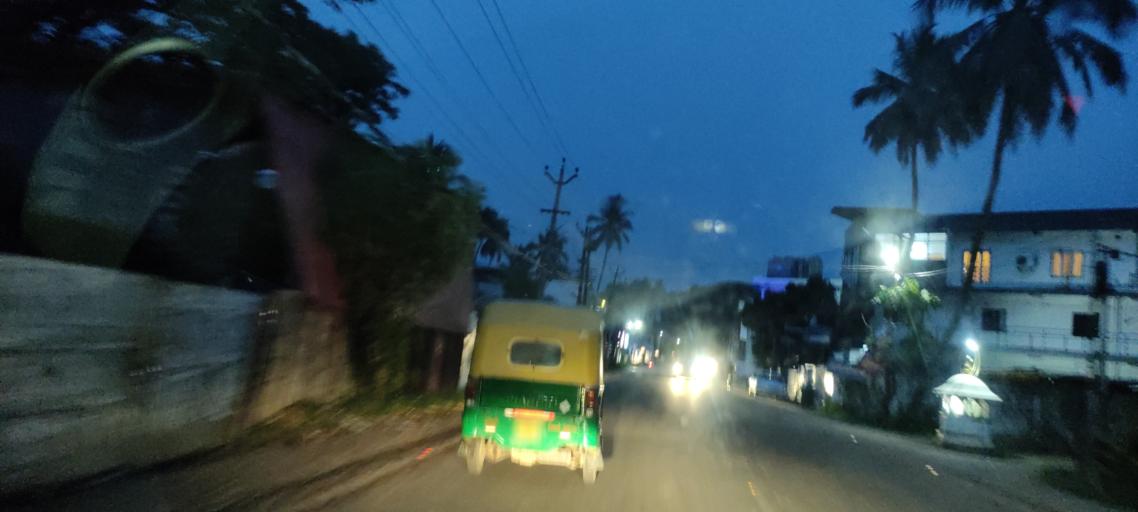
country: IN
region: Kerala
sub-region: Alappuzha
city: Arukutti
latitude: 9.8845
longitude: 76.3009
